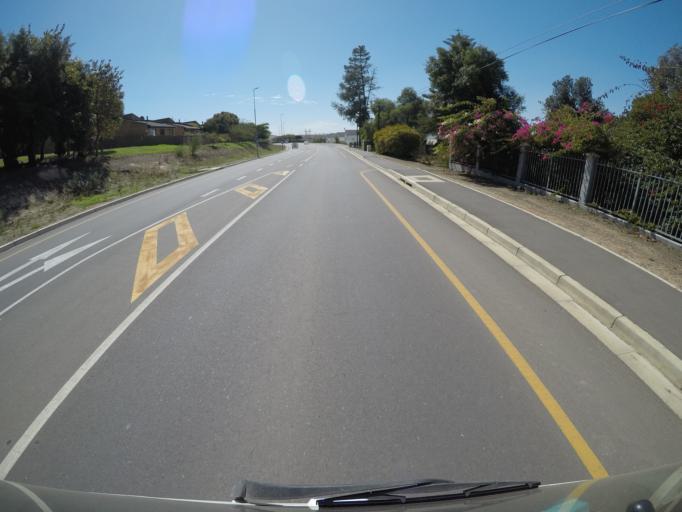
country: ZA
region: Western Cape
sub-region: City of Cape Town
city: Kraaifontein
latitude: -33.8256
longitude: 18.6370
